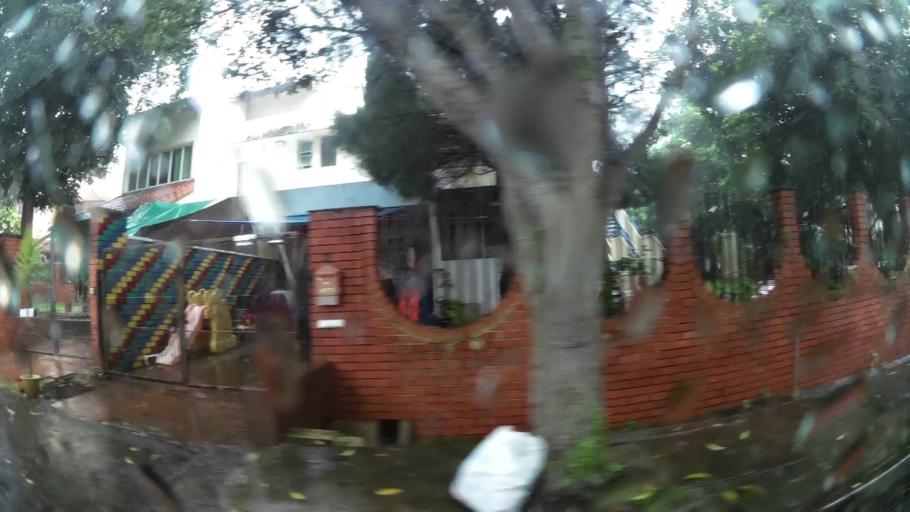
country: SG
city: Singapore
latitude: 1.3395
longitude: 103.9587
